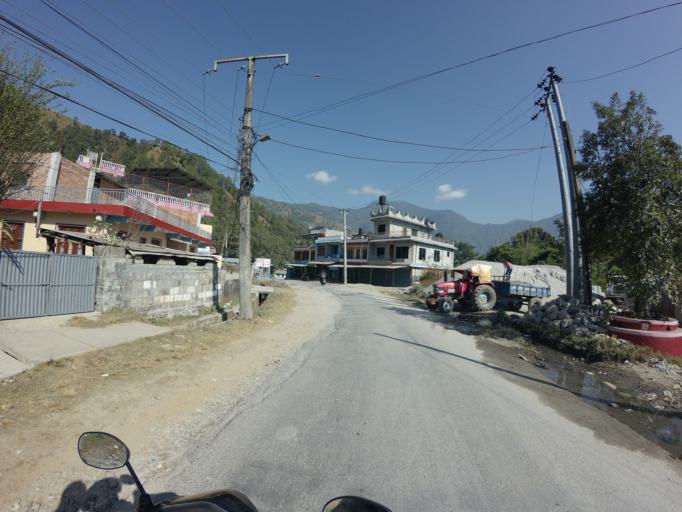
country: NP
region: Western Region
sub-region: Gandaki Zone
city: Pokhara
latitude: 28.2707
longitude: 83.9800
